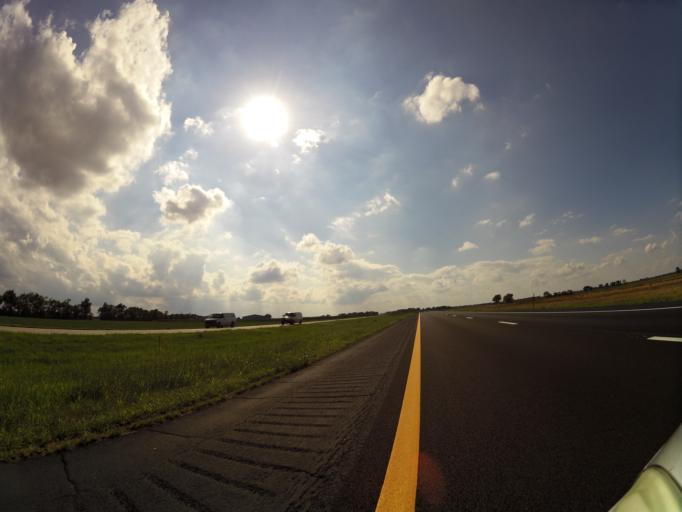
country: US
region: Kansas
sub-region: Reno County
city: Haven
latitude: 37.8772
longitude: -97.7039
